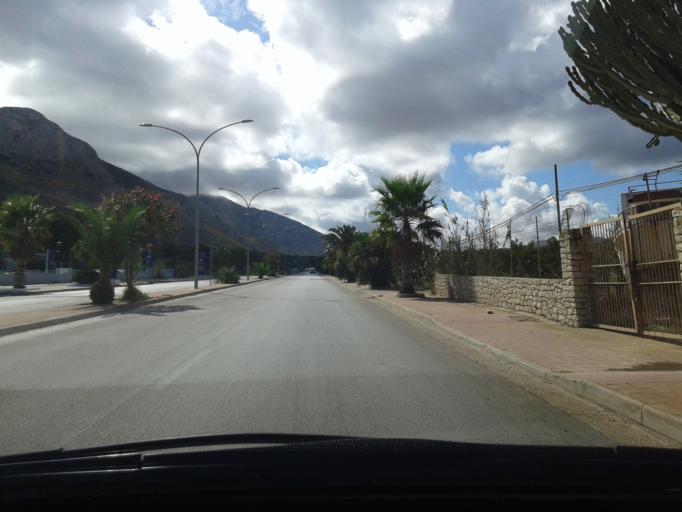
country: IT
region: Sicily
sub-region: Trapani
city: San Vito Lo Capo
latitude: 38.1648
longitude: 12.7359
